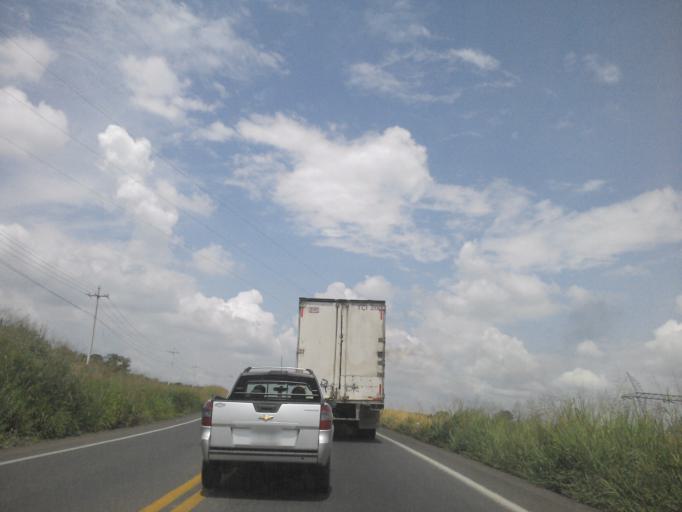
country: MX
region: Jalisco
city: Acatic
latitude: 20.6987
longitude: -102.9742
